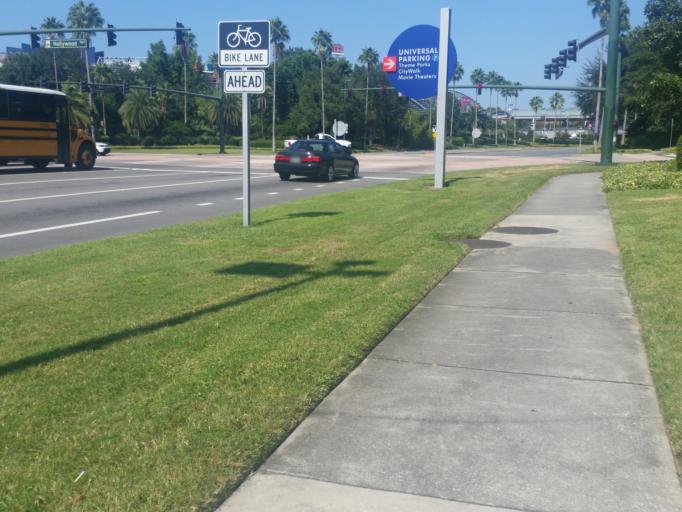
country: US
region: Florida
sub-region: Orange County
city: Tangelo Park
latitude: 28.4706
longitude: -81.4646
